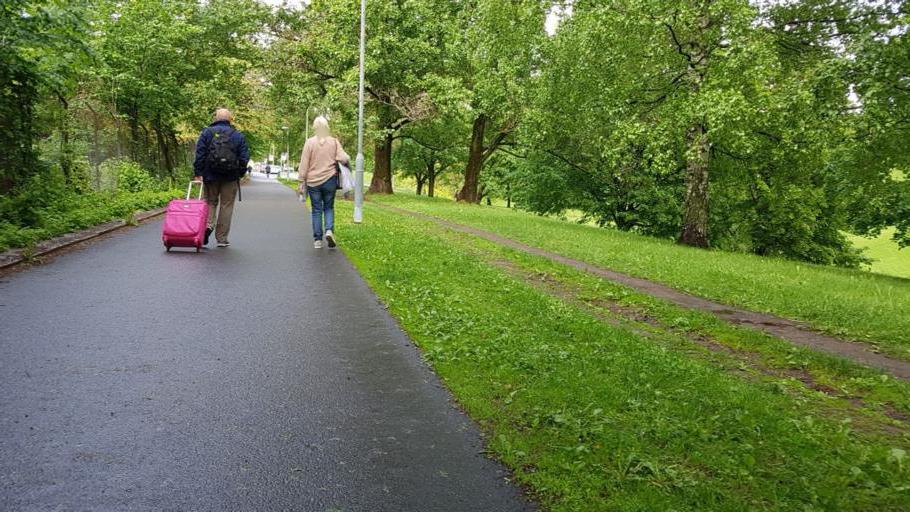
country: NO
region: Oslo
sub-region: Oslo
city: Oslo
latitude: 59.9326
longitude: 10.7737
